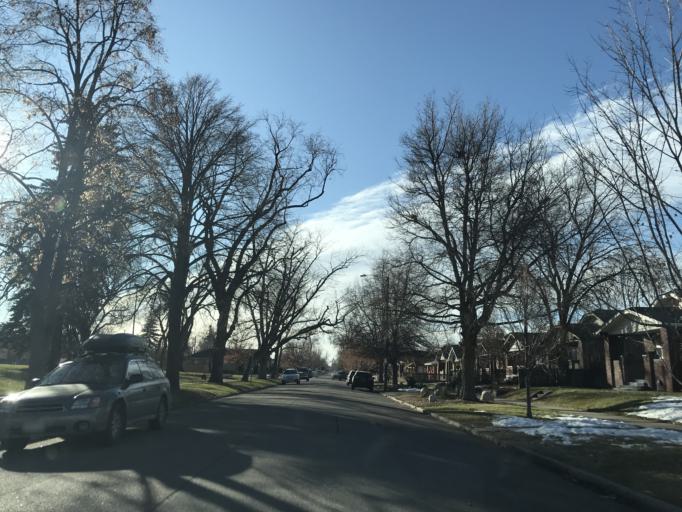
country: US
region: Colorado
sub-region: Denver County
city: Denver
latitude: 39.7680
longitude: -104.9623
